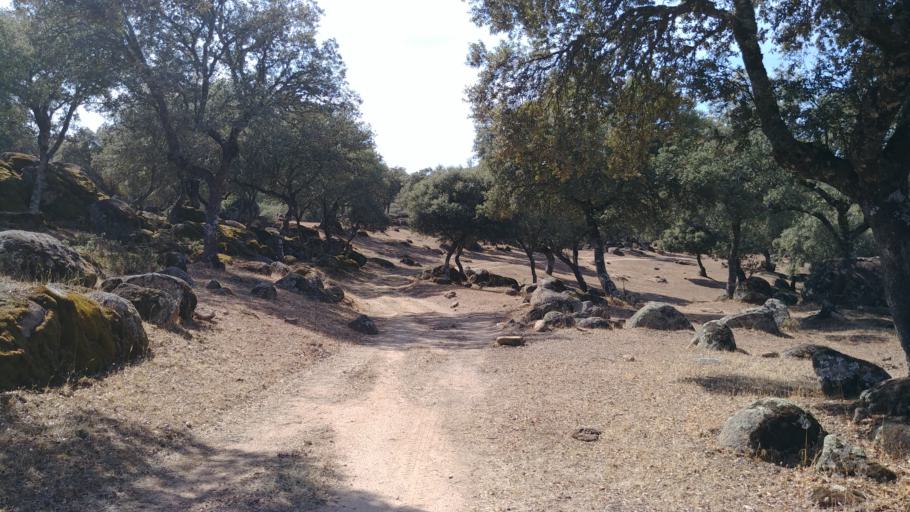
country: ES
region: Castille-La Mancha
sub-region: Province of Toledo
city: Navalcan
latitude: 40.0518
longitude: -5.1404
